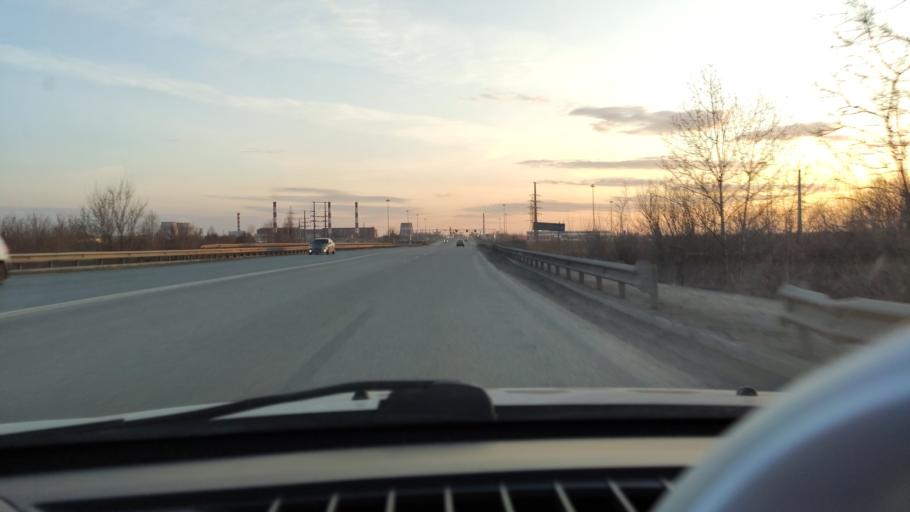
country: RU
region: Perm
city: Kondratovo
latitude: 57.9395
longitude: 56.1674
